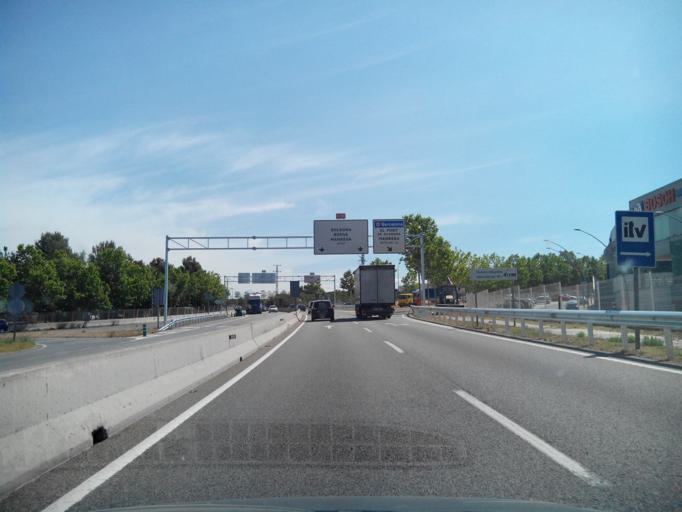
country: ES
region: Catalonia
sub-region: Provincia de Barcelona
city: Manresa
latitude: 41.7170
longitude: 1.8433
